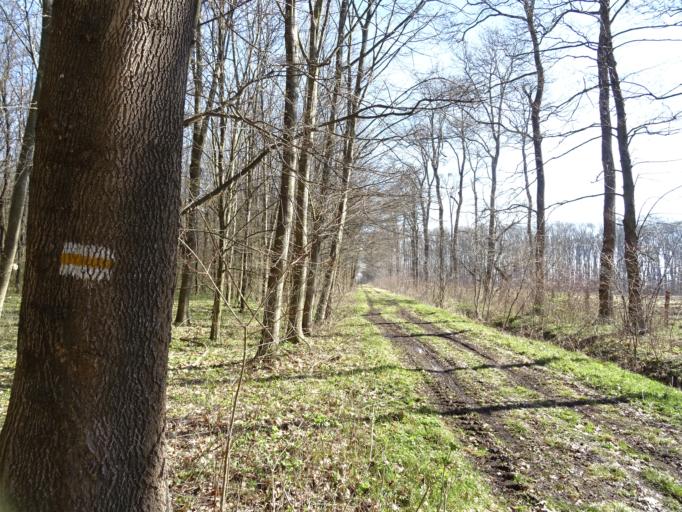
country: HU
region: Gyor-Moson-Sopron
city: Mihalyi
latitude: 47.5229
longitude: 17.0524
